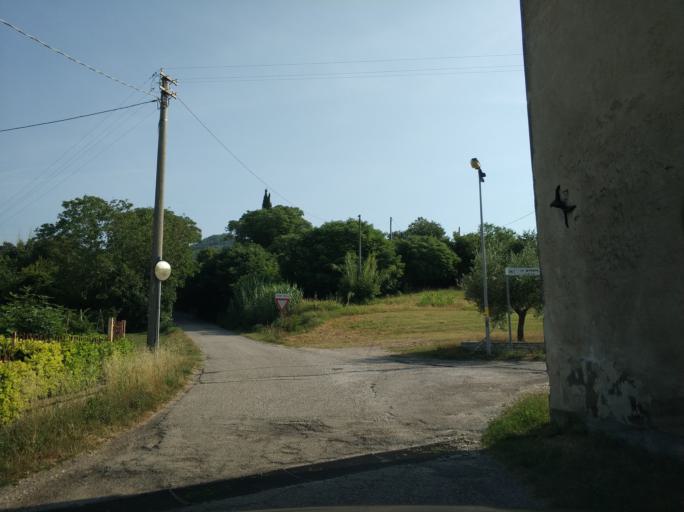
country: IT
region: Veneto
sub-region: Provincia di Padova
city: Baone
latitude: 45.2354
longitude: 11.6936
